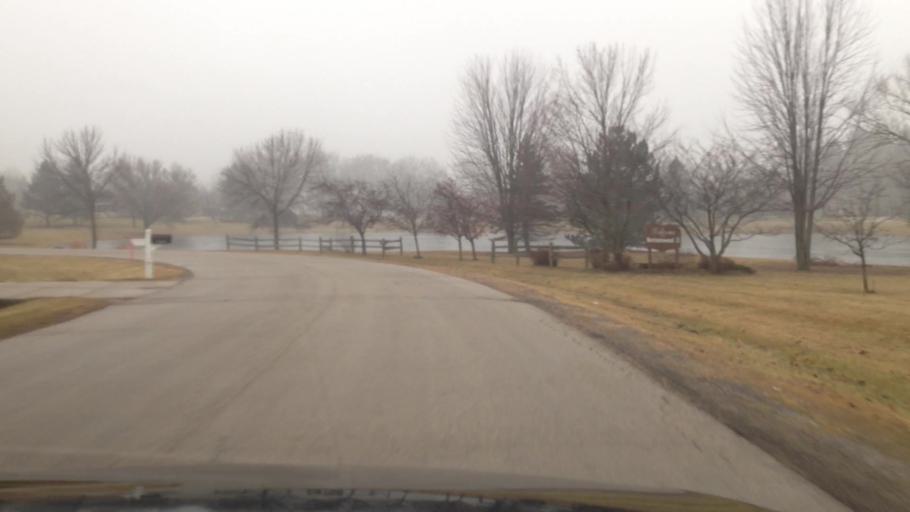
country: US
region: Wisconsin
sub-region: Waukesha County
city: Muskego
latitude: 42.9113
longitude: -88.0930
